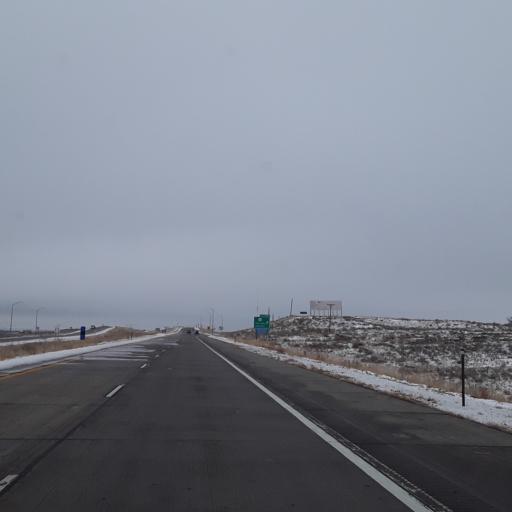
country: US
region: Colorado
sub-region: Logan County
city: Sterling
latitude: 40.6135
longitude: -103.1761
